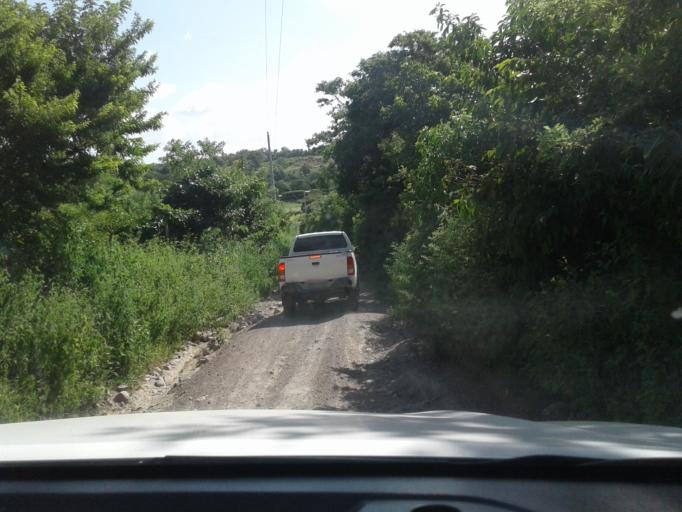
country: NI
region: Matagalpa
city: Terrabona
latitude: 12.5532
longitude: -86.0199
